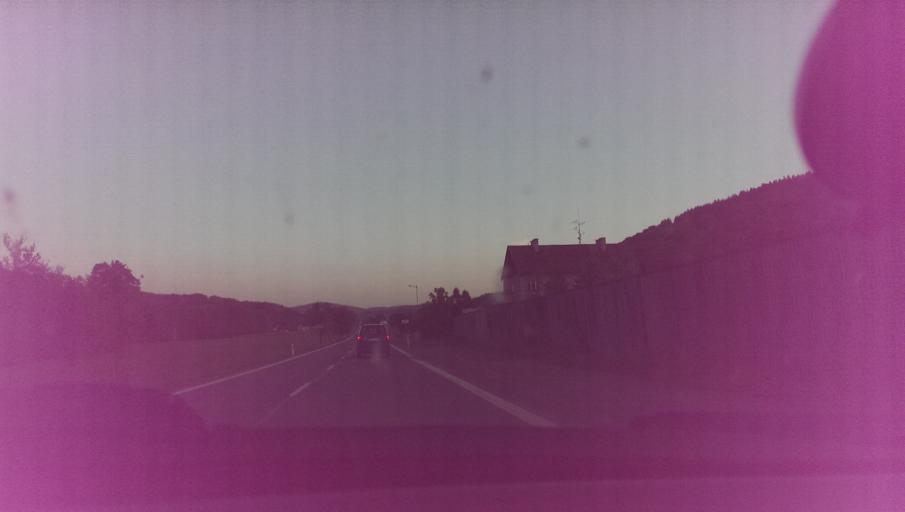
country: CZ
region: Zlin
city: Valasska Polanka
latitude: 49.2988
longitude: 18.0015
